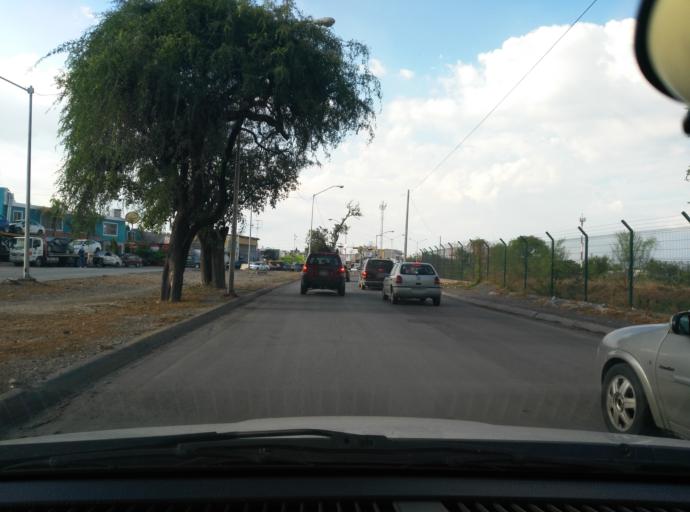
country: MX
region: Nuevo Leon
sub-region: Apodaca
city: Fraccionamiento Cosmopolis Octavo Sector
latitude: 25.7662
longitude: -100.2423
